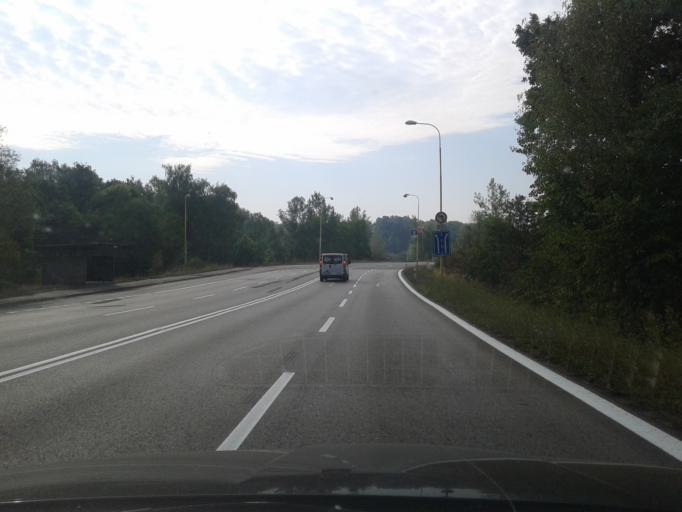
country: CZ
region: Moravskoslezsky
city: Havirov
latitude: 49.8045
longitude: 18.4416
